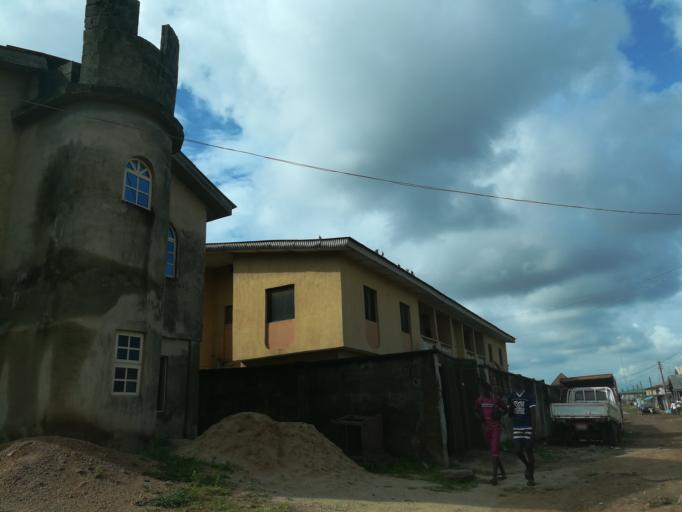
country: NG
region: Lagos
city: Ebute Ikorodu
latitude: 6.5936
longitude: 3.5072
